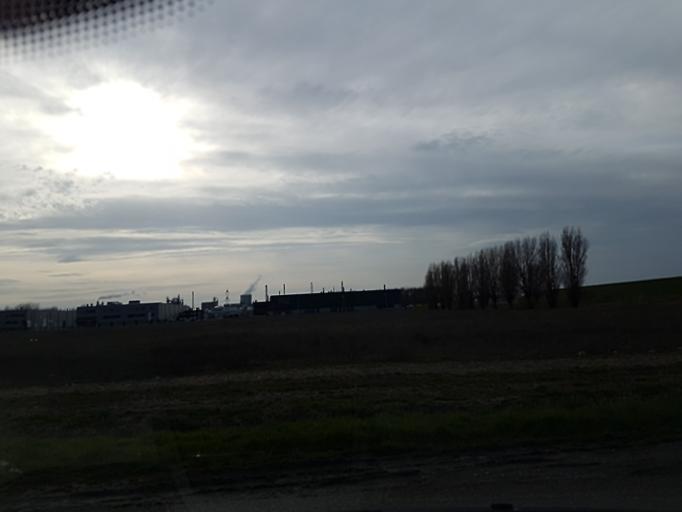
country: NL
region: Zeeland
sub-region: Gemeente Terneuzen
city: Terneuzen
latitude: 51.3422
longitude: 3.8054
